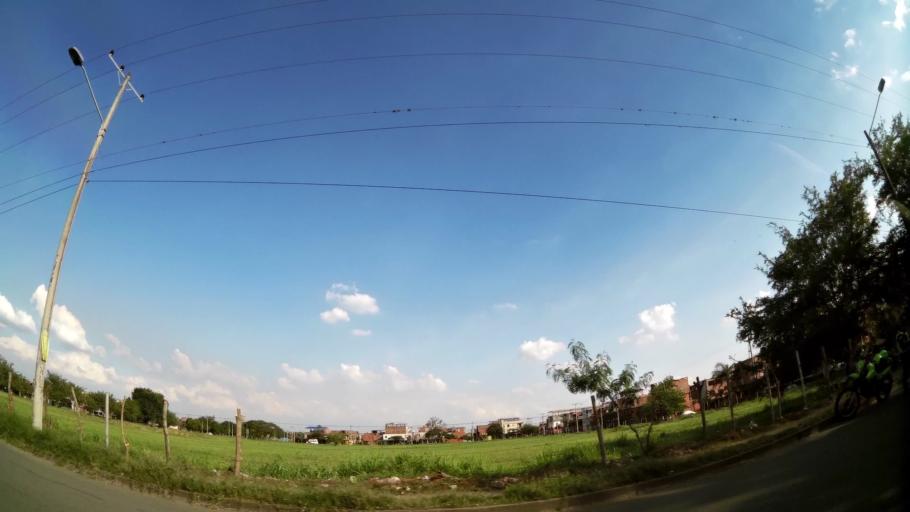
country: CO
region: Valle del Cauca
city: Cali
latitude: 3.3978
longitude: -76.5088
